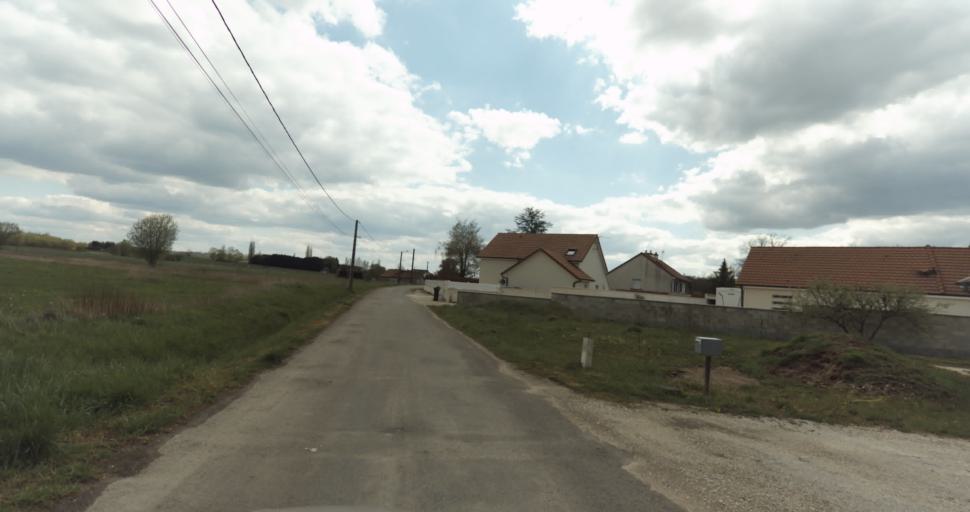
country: FR
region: Bourgogne
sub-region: Departement de la Cote-d'Or
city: Auxonne
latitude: 47.1800
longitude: 5.3927
